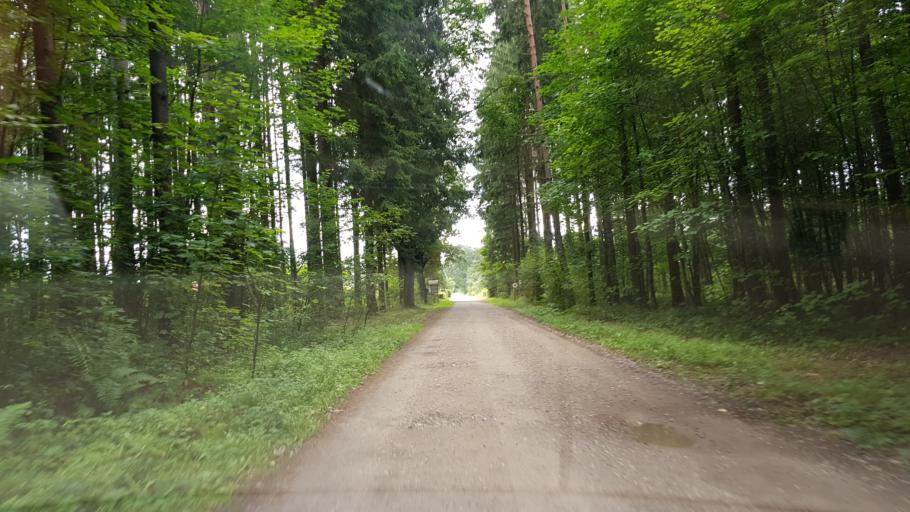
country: PL
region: West Pomeranian Voivodeship
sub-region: Powiat bialogardzki
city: Tychowo
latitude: 53.9999
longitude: 16.3042
